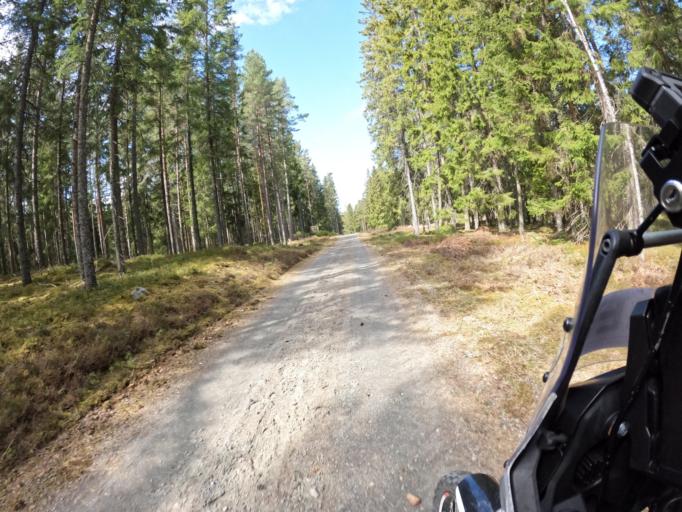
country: SE
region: Joenkoeping
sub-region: Mullsjo Kommun
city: Mullsjoe
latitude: 57.9448
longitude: 13.6950
